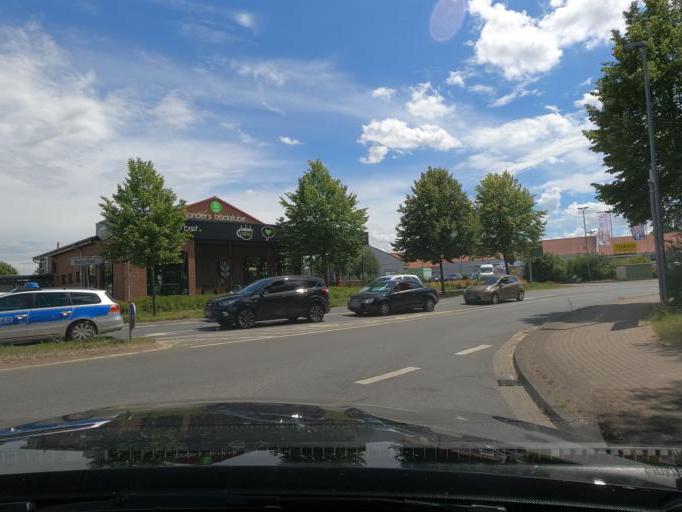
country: DE
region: Lower Saxony
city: Lengede
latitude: 52.1929
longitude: 10.3263
